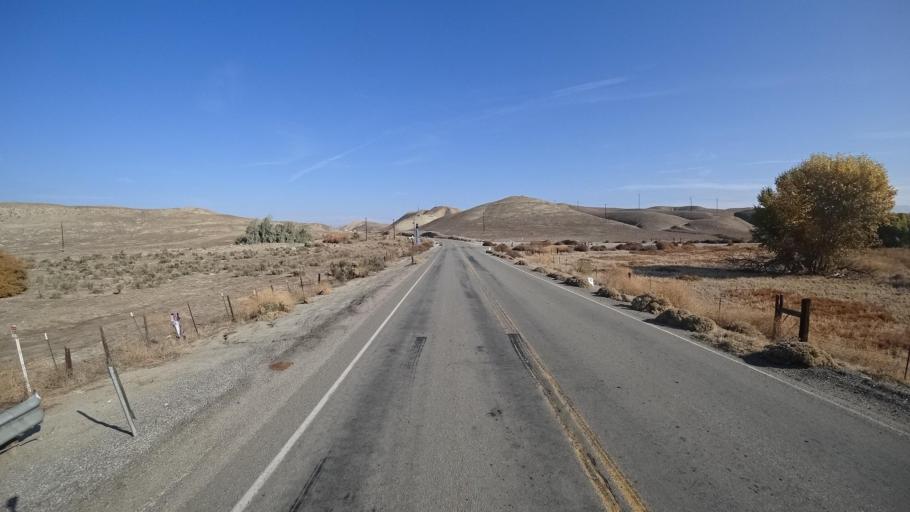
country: US
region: California
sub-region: Kern County
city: Oildale
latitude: 35.5296
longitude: -118.9626
